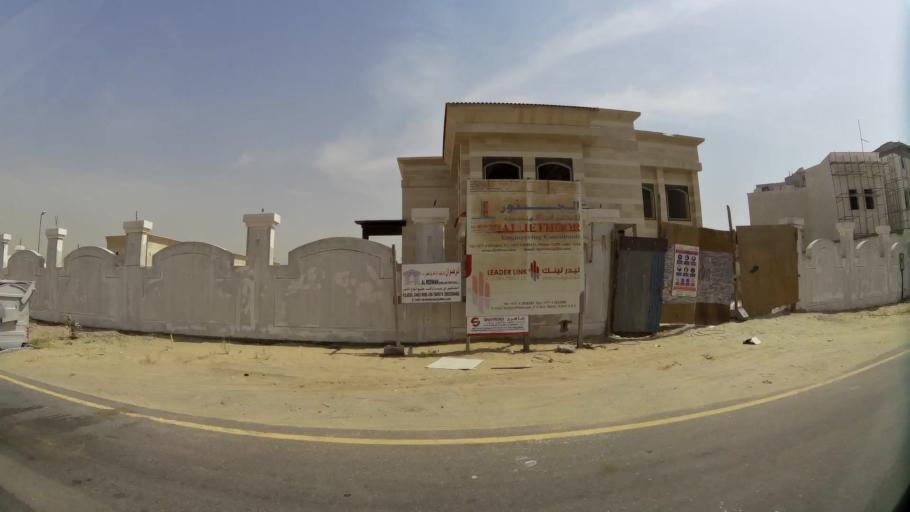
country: AE
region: Ash Shariqah
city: Sharjah
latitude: 25.2505
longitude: 55.4877
